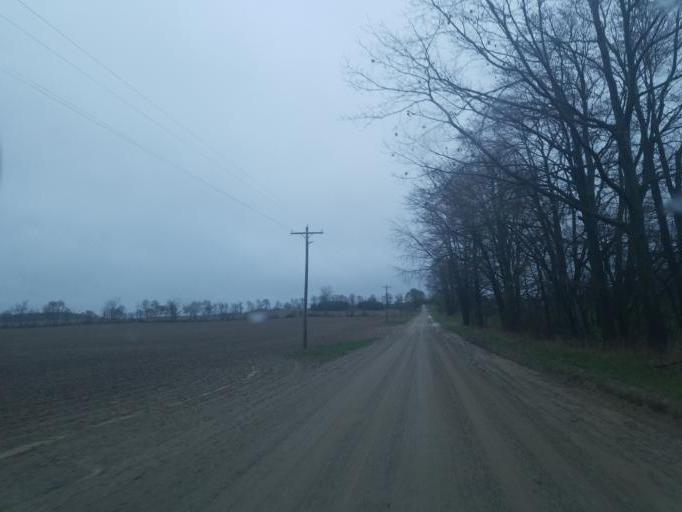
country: US
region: Michigan
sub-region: Montcalm County
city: Edmore
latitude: 43.4660
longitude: -85.0238
